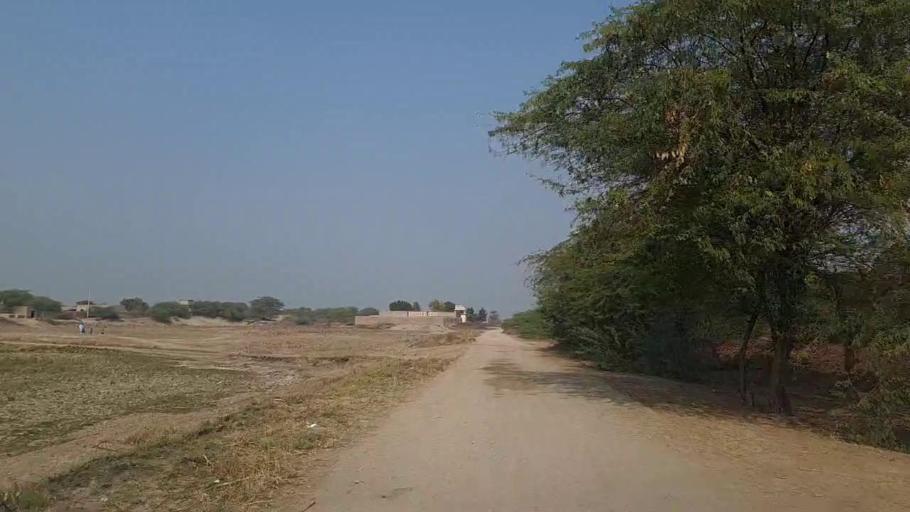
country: PK
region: Sindh
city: Daur
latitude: 26.4412
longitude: 68.4428
